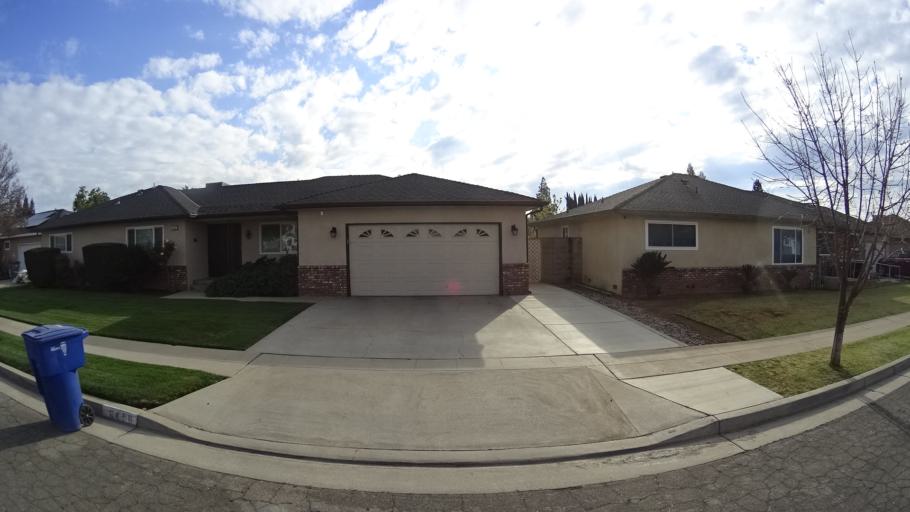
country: US
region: California
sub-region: Fresno County
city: Clovis
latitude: 36.8319
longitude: -119.7679
